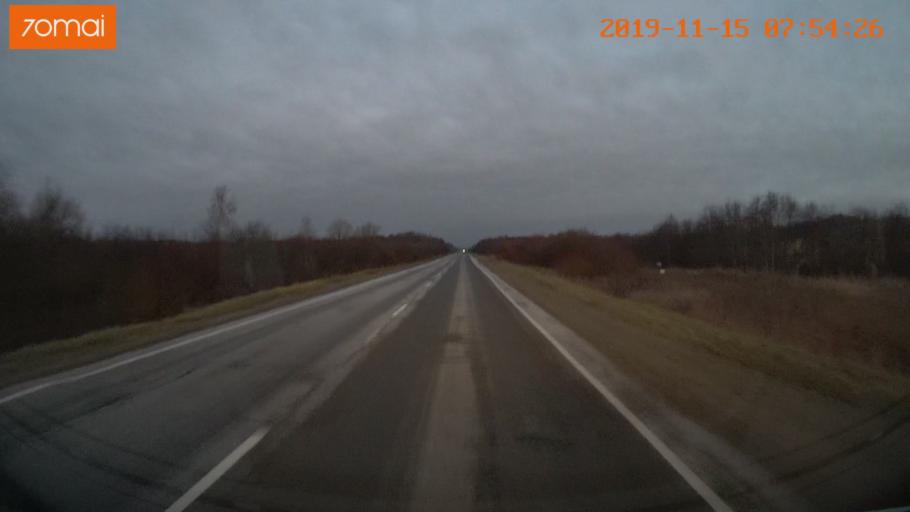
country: RU
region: Vologda
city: Cherepovets
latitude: 58.8981
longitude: 38.1764
